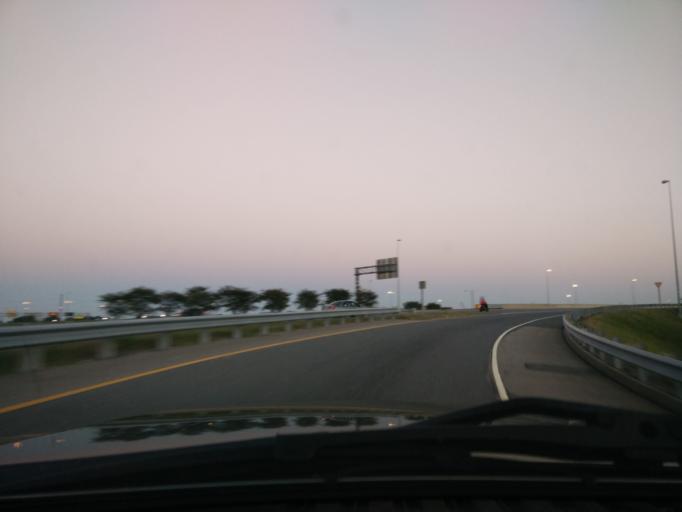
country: US
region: Virginia
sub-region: City of Chesapeake
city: Chesapeake
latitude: 36.7751
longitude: -76.2558
